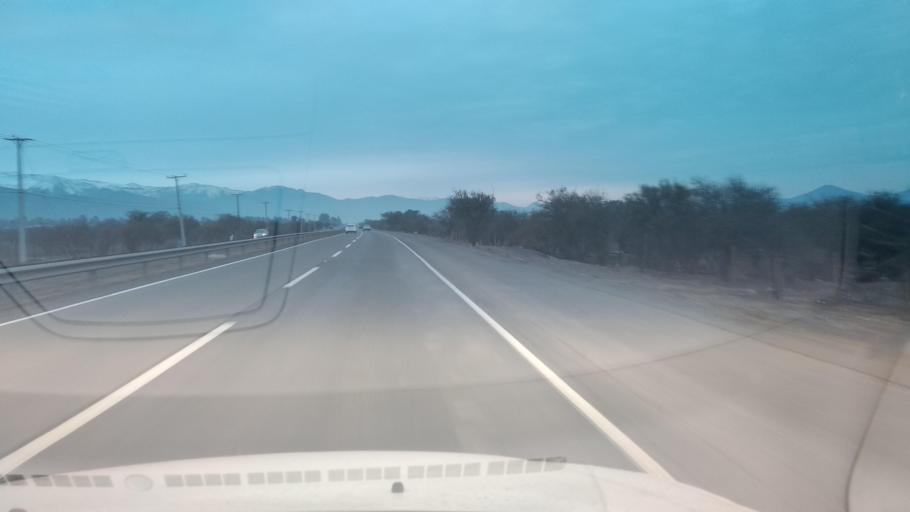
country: CL
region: Santiago Metropolitan
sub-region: Provincia de Chacabuco
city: Chicureo Abajo
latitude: -33.1285
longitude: -70.6722
